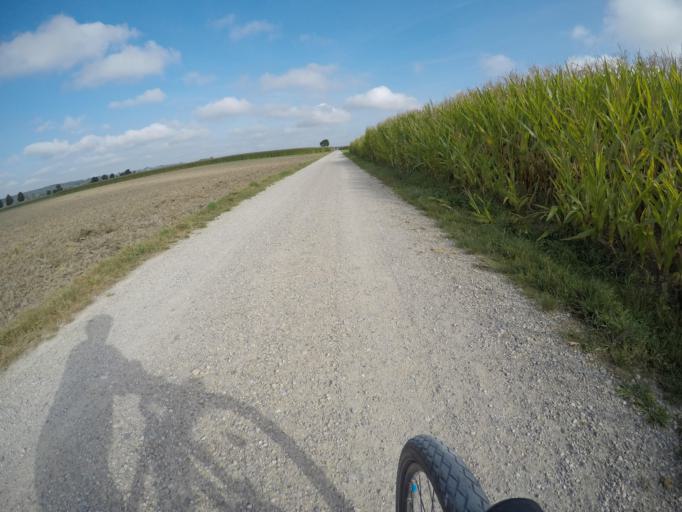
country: DE
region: Bavaria
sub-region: Swabia
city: Meitingen
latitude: 48.5623
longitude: 10.8518
